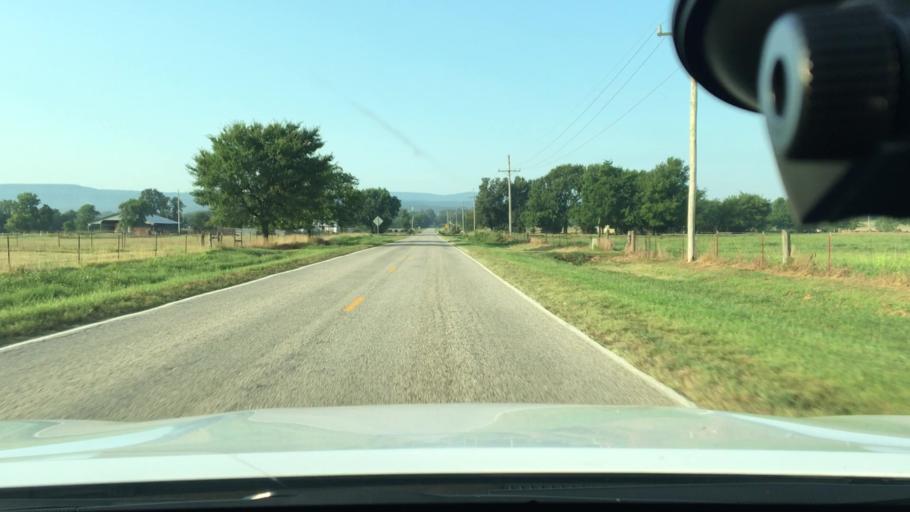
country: US
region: Arkansas
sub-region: Logan County
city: Paris
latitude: 35.3286
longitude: -93.6321
